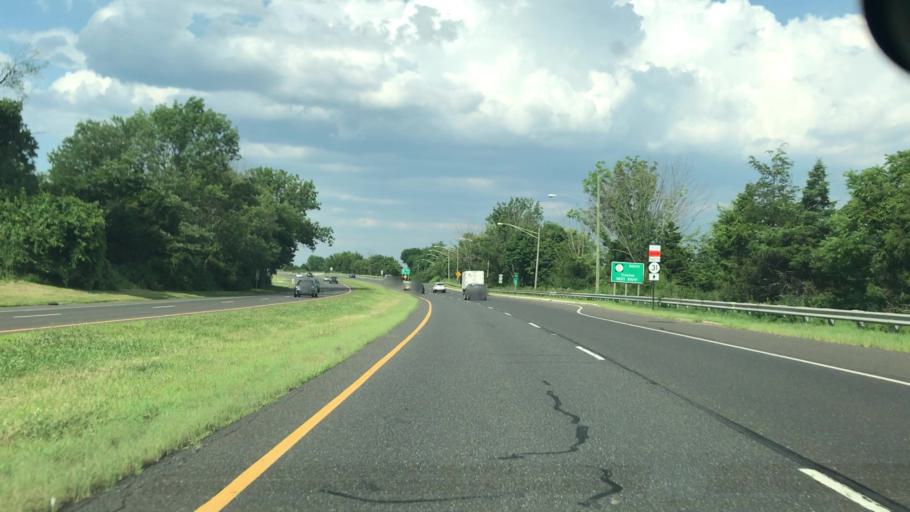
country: US
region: New Jersey
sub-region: Hunterdon County
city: Lambertville
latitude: 40.4207
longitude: -74.8694
